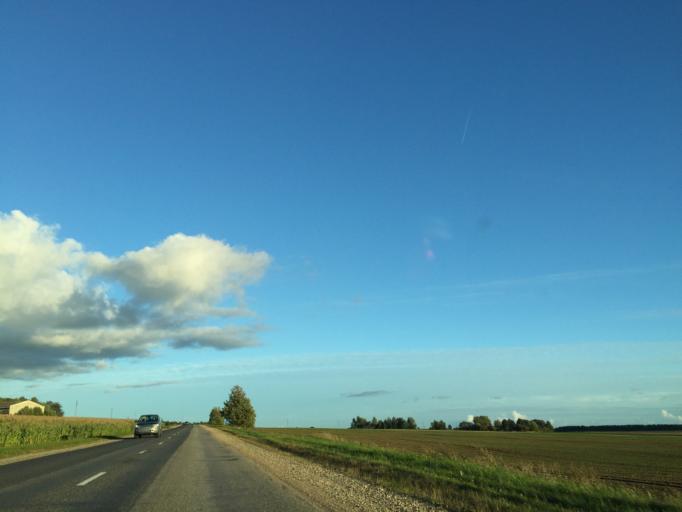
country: LV
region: Saldus Rajons
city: Saldus
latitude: 56.7087
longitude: 22.4188
